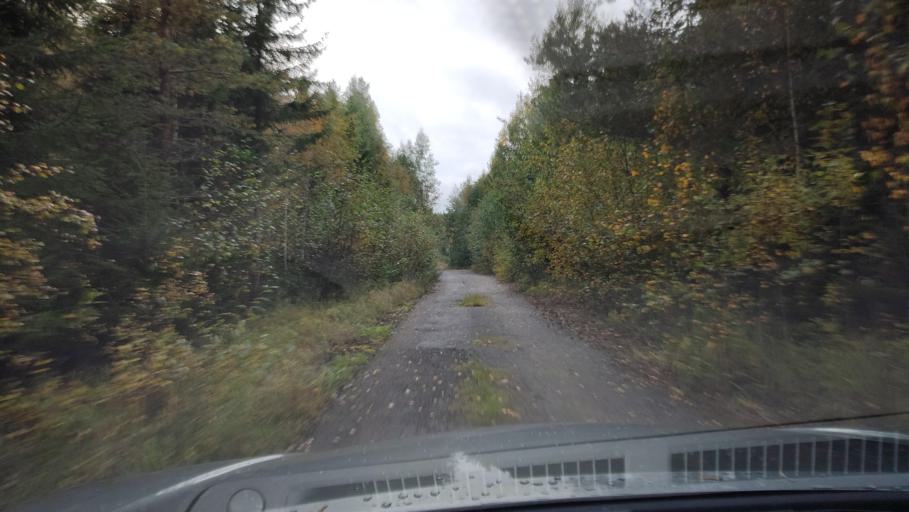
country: FI
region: Ostrobothnia
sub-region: Sydosterbotten
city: Kristinestad
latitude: 62.2691
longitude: 21.4552
